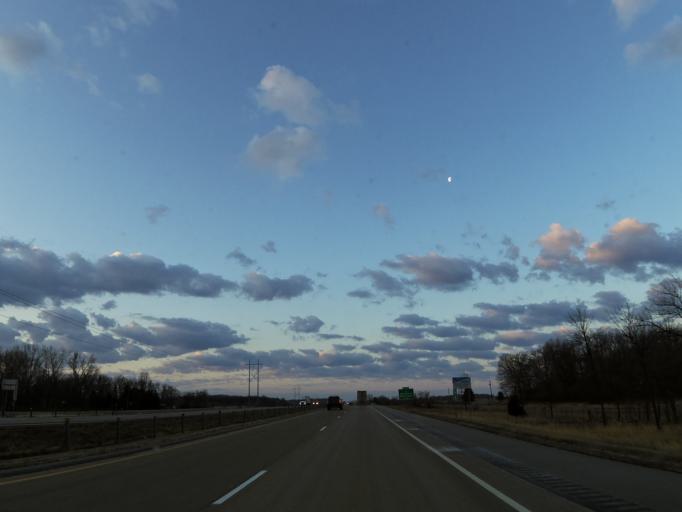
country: US
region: Minnesota
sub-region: Scott County
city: Elko New Market
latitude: 44.4921
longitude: -93.2919
